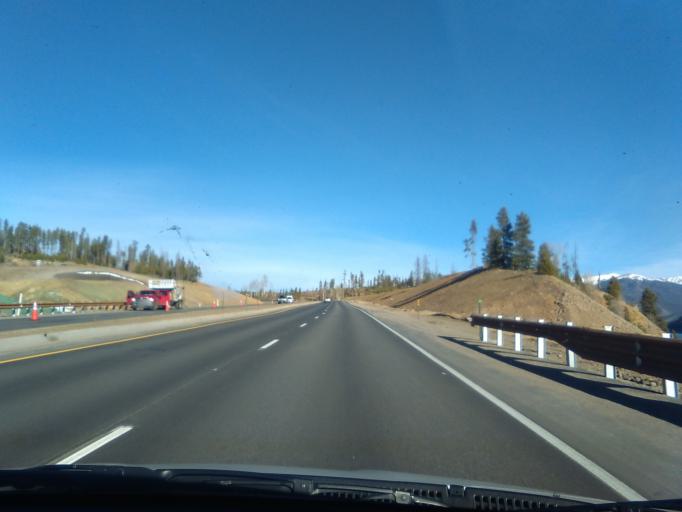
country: US
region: Colorado
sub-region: Summit County
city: Frisco
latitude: 39.5702
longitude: -106.0569
